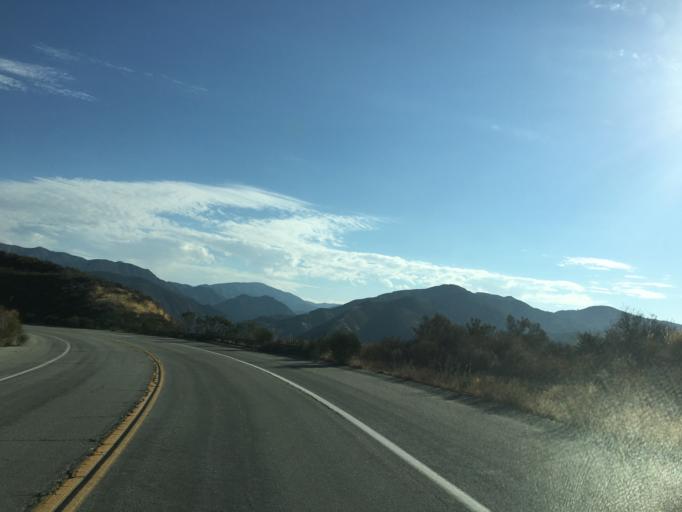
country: US
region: California
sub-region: Los Angeles County
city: Castaic
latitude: 34.5904
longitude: -118.6705
